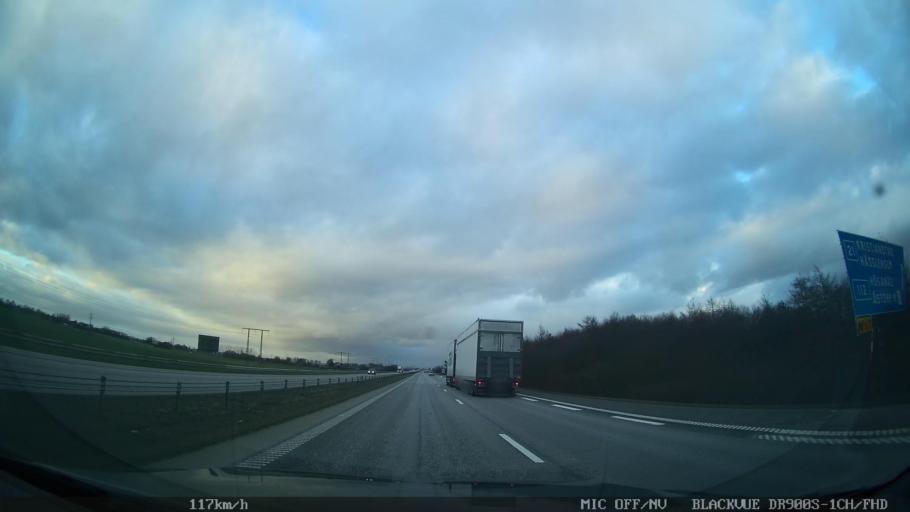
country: SE
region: Skane
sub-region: Astorps Kommun
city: Astorp
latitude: 56.1420
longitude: 12.9317
